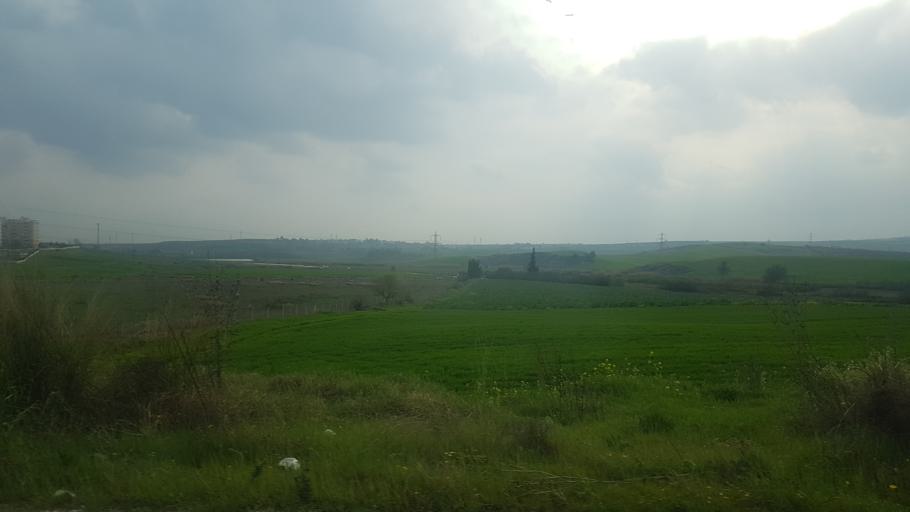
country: TR
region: Mersin
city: Yenice
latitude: 37.0530
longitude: 35.1718
